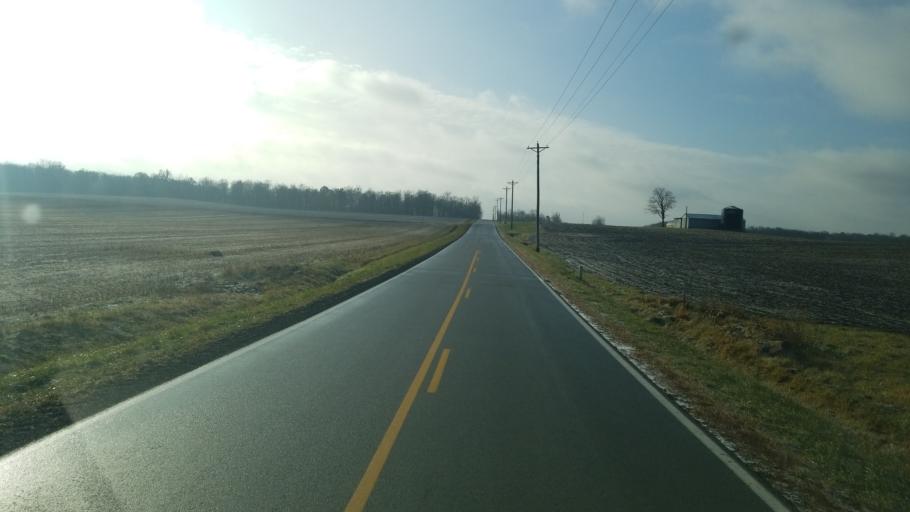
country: US
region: Ohio
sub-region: Richland County
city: Shelby
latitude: 40.9220
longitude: -82.7434
